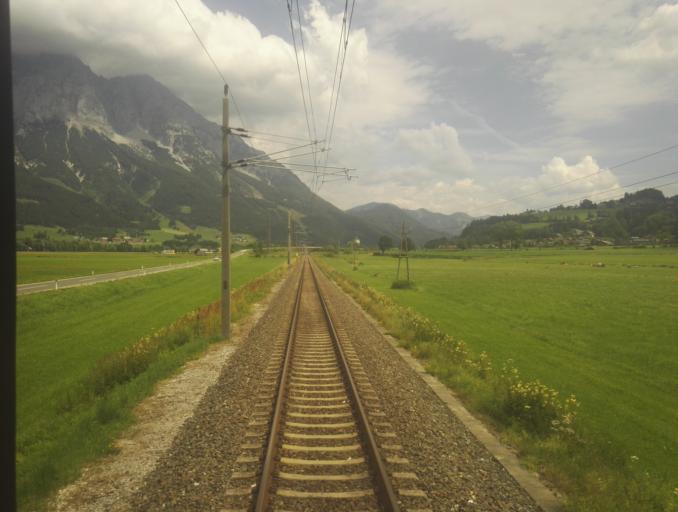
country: AT
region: Styria
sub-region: Politischer Bezirk Liezen
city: Niederoblarn
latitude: 47.4722
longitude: 14.0097
